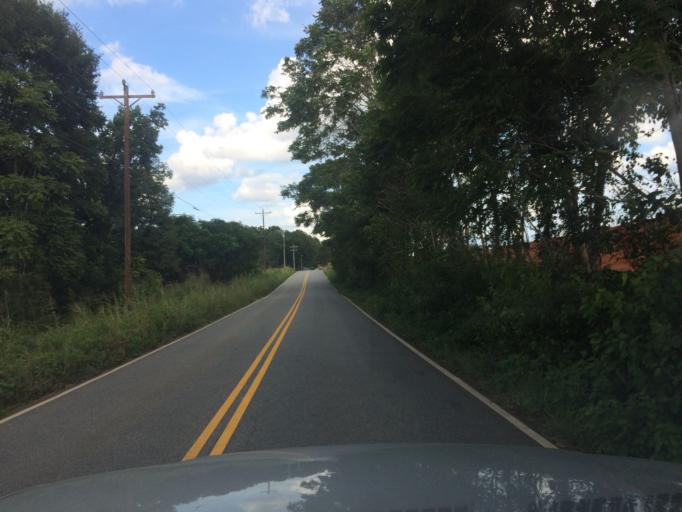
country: US
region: South Carolina
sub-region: Spartanburg County
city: Duncan
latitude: 34.8612
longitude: -82.1395
